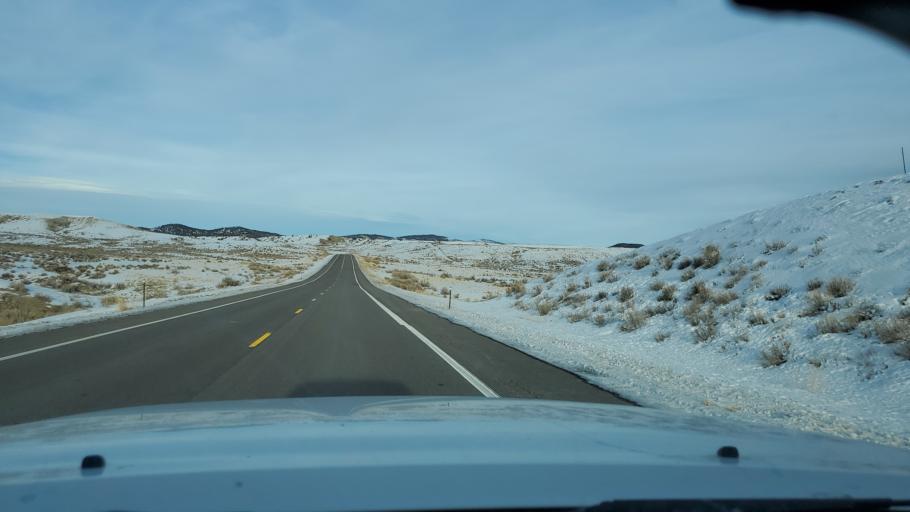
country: US
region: Colorado
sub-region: Rio Blanco County
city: Rangely
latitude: 40.3157
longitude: -108.5153
